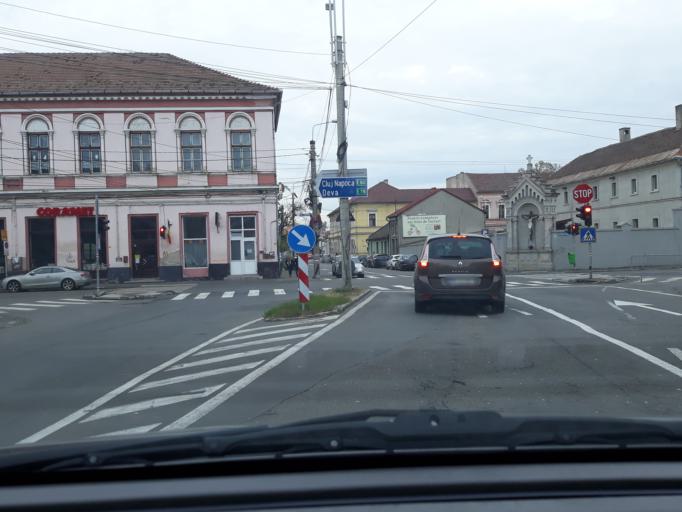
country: RO
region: Bihor
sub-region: Comuna Biharea
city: Oradea
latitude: 47.0531
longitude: 21.9326
